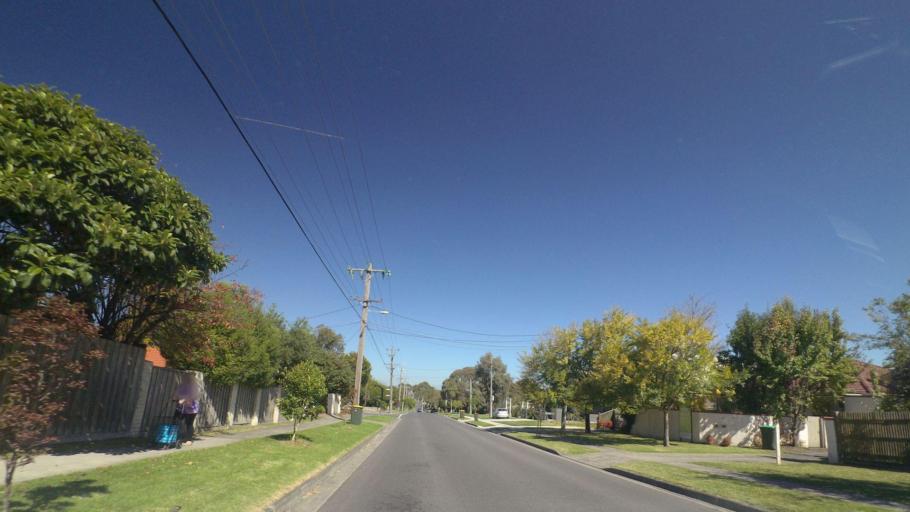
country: AU
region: Victoria
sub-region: Manningham
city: Donvale
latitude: -37.7927
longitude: 145.1705
